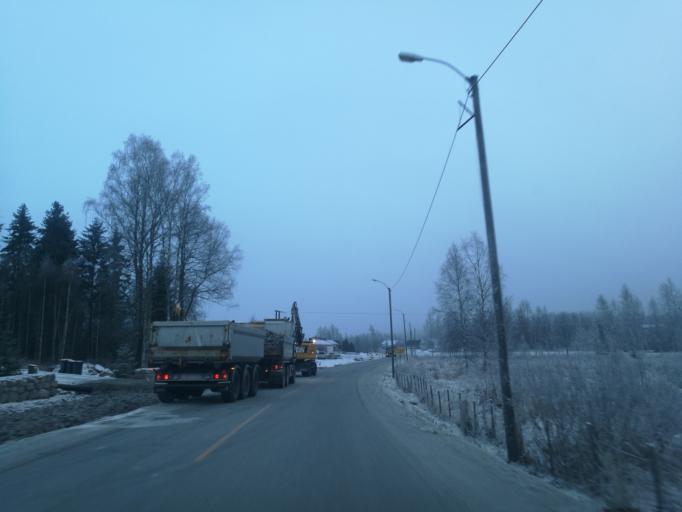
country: NO
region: Hedmark
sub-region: Kongsvinger
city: Kongsvinger
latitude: 60.2581
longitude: 12.0733
